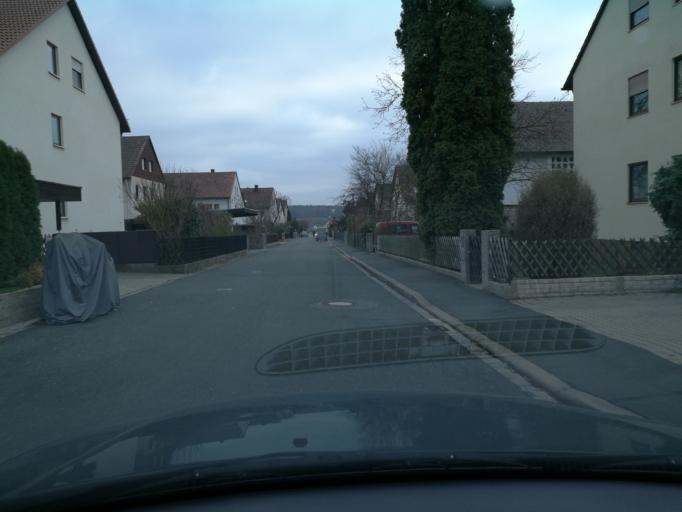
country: DE
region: Bavaria
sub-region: Regierungsbezirk Mittelfranken
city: Seukendorf
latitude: 49.4870
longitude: 10.8866
